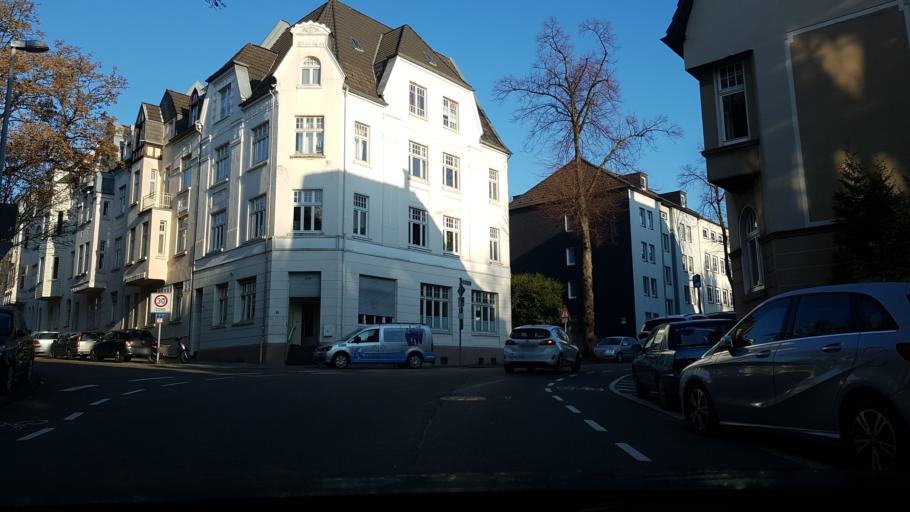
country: DE
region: North Rhine-Westphalia
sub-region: Regierungsbezirk Dusseldorf
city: Muelheim (Ruhr)
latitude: 51.4297
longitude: 6.8952
